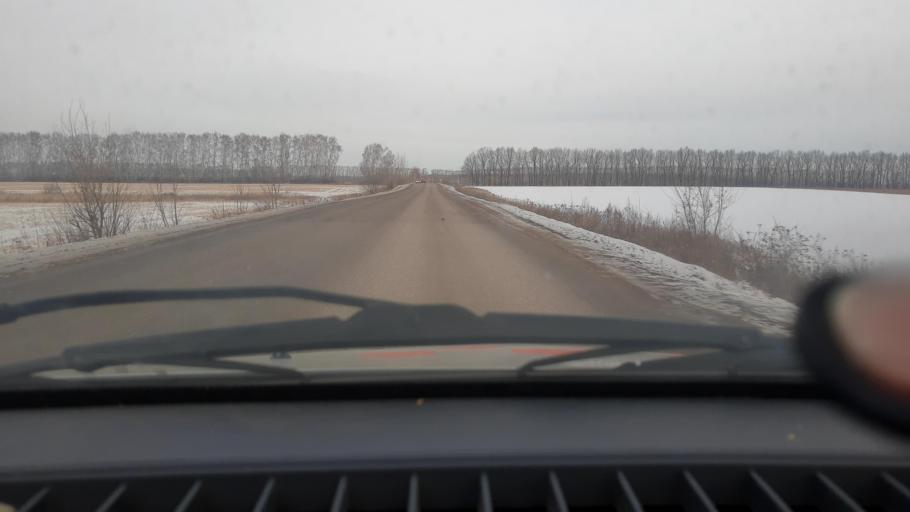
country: RU
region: Bashkortostan
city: Mikhaylovka
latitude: 54.8820
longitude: 55.8565
